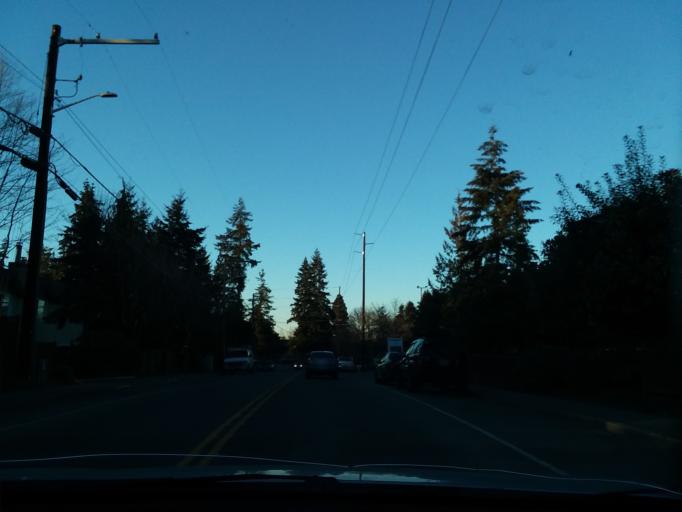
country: US
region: Washington
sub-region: Snohomish County
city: Mountlake Terrace
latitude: 47.8050
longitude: -122.2978
